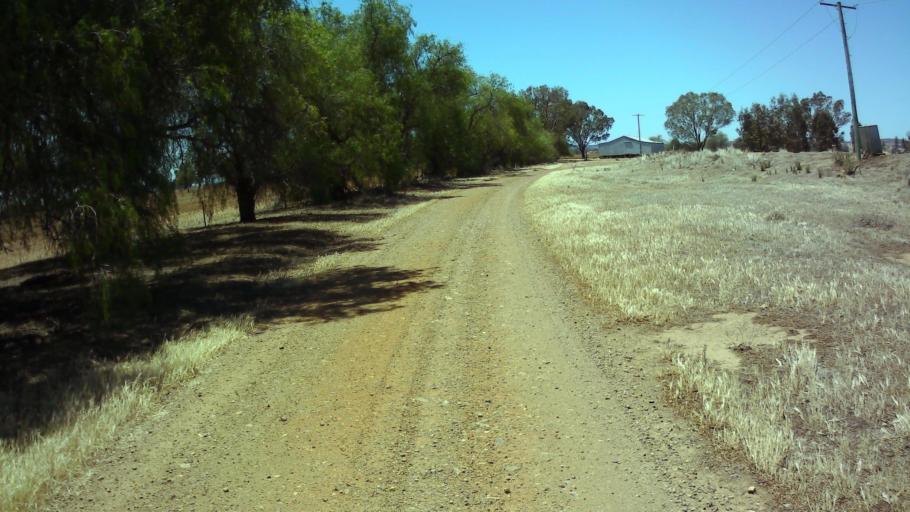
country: AU
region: New South Wales
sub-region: Weddin
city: Grenfell
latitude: -33.7334
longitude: 148.0972
